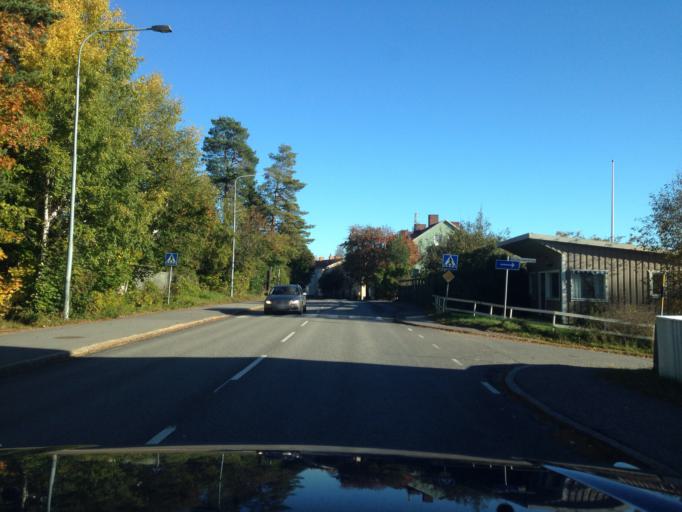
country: SE
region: Vaesternorrland
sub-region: Sundsvalls Kommun
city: Sundsvall
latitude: 62.3987
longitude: 17.3242
